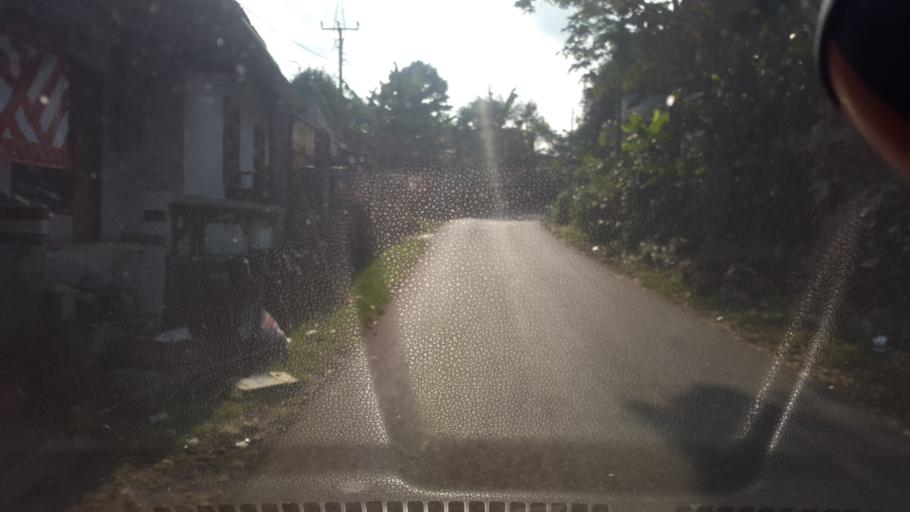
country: ID
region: West Java
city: Cicurug
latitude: -6.8470
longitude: 106.7264
